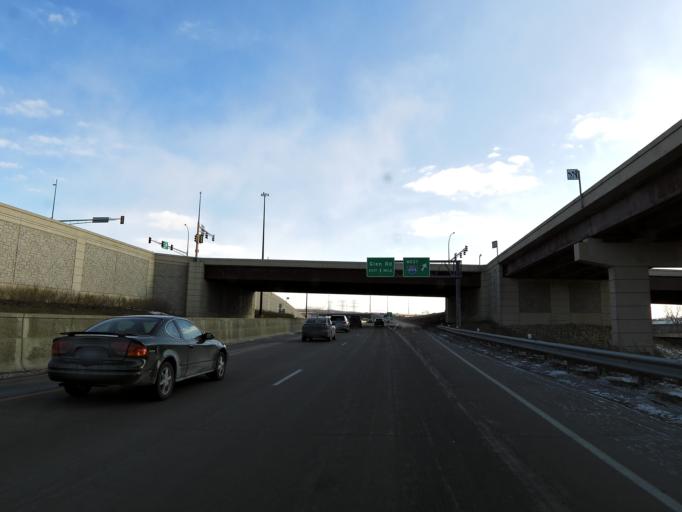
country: US
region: Minnesota
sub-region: Washington County
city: Newport
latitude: 44.8920
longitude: -93.0073
